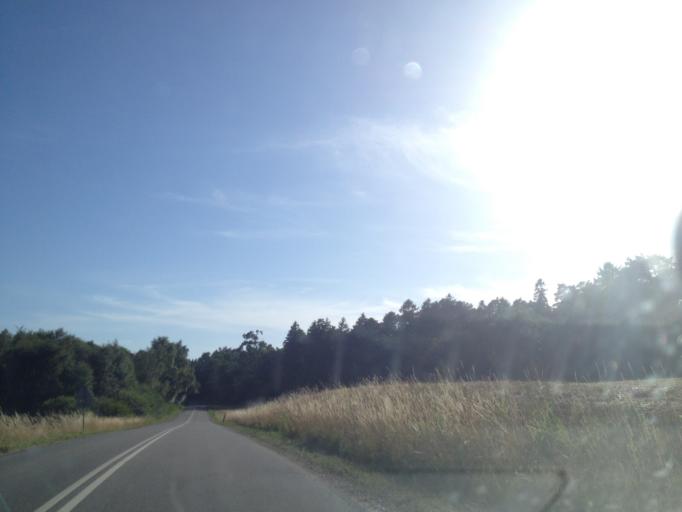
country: DK
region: Capital Region
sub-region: Halsnaes Kommune
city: Frederiksvaerk
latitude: 56.0292
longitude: 12.0861
